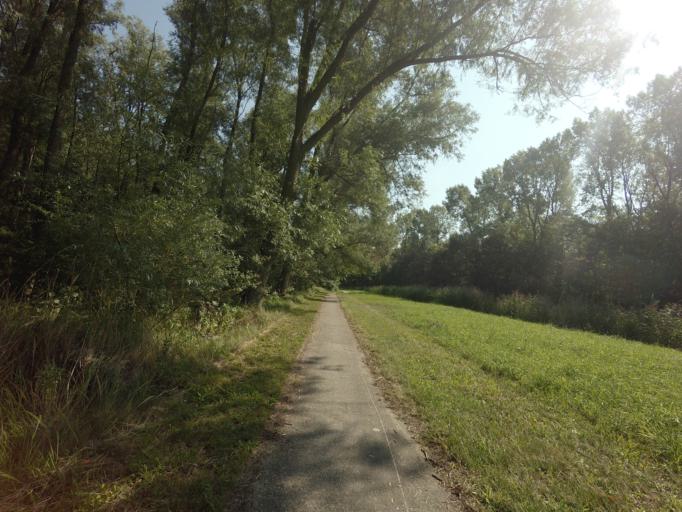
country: NL
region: Groningen
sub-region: Gemeente De Marne
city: Ulrum
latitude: 53.3907
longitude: 6.2588
